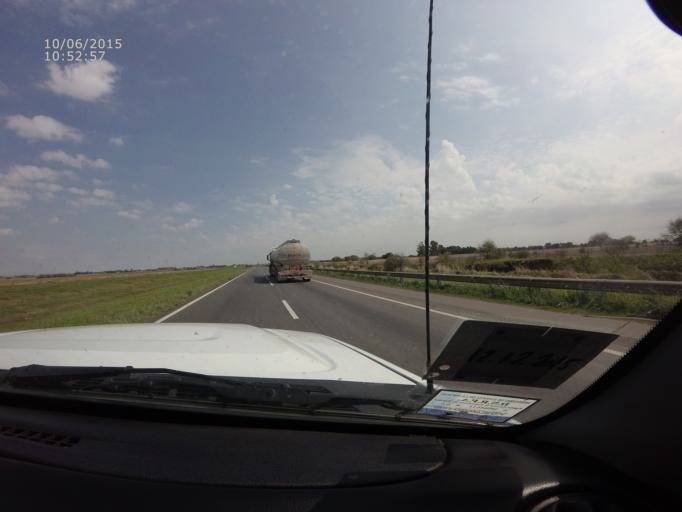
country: AR
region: Buenos Aires
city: San Nicolas de los Arroyos
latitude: -33.3467
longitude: -60.2781
